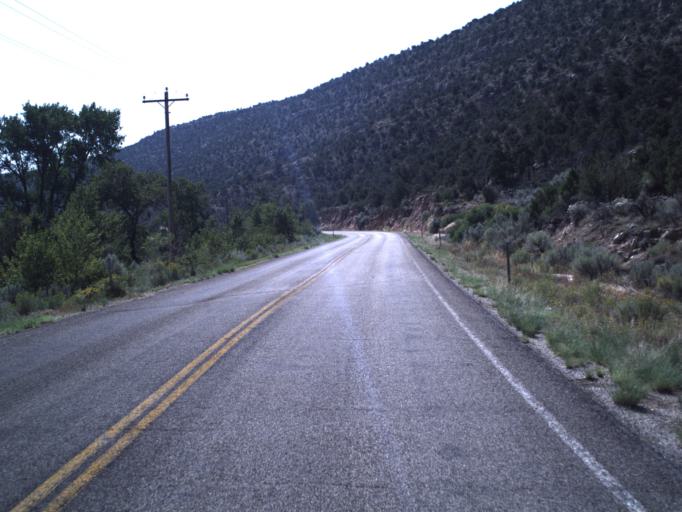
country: US
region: Utah
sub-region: Duchesne County
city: Duchesne
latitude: 40.2873
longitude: -110.4966
